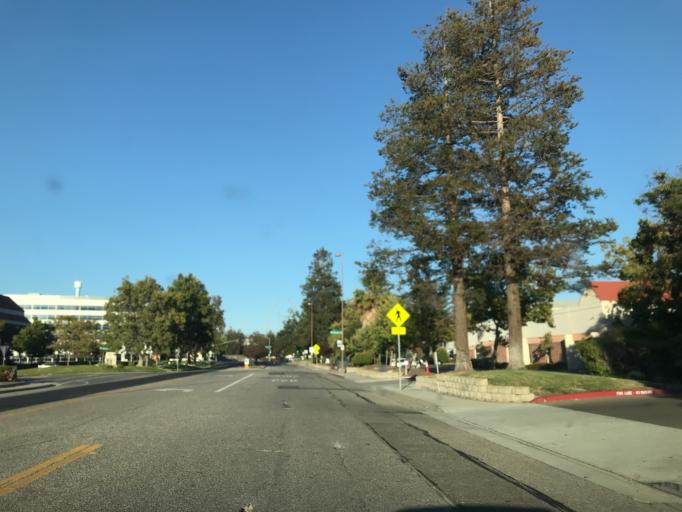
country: US
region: California
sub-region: Santa Clara County
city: Santa Clara
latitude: 37.3959
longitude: -121.9804
